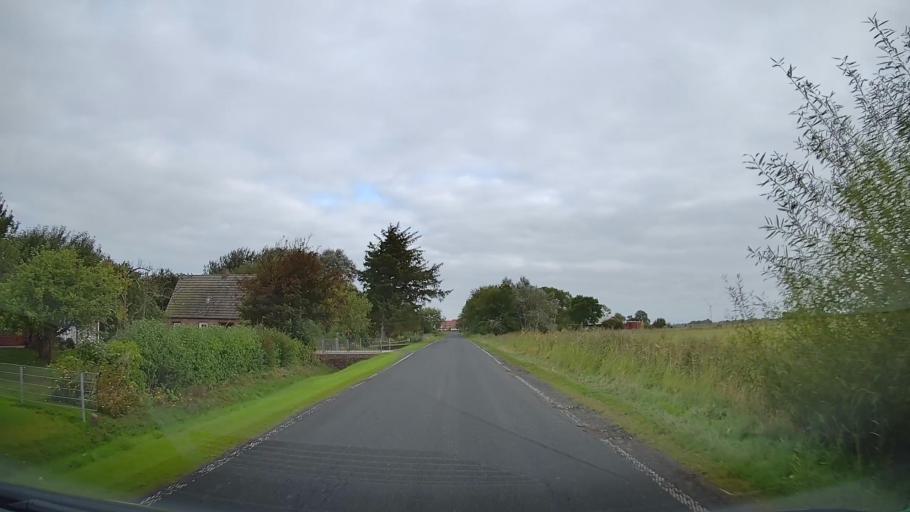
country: DE
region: Schleswig-Holstein
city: Friedrich-Wilhelm-Lubke-Koog
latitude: 54.8301
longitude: 8.6560
